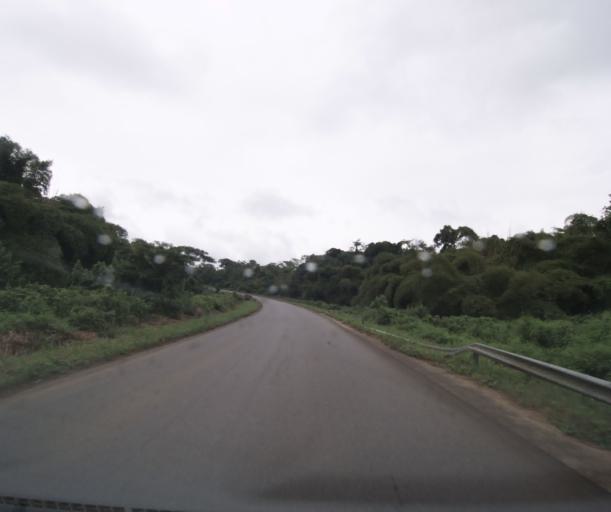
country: CM
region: Littoral
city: Edea
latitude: 3.7210
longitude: 10.1076
